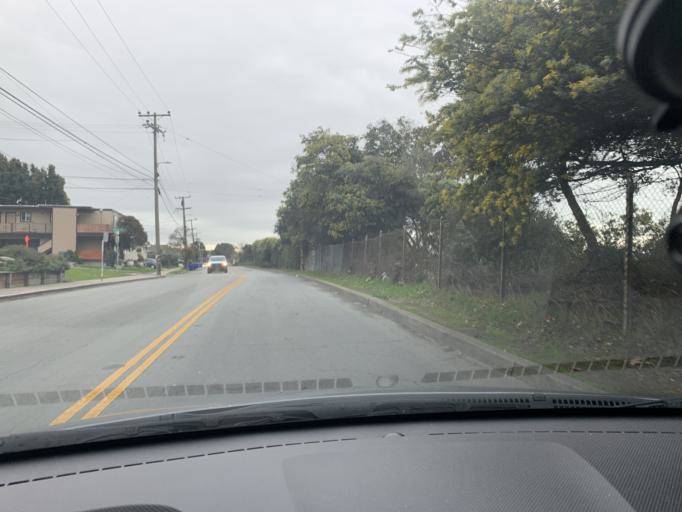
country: US
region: California
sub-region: Contra Costa County
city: Rollingwood
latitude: 37.9558
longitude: -122.3290
